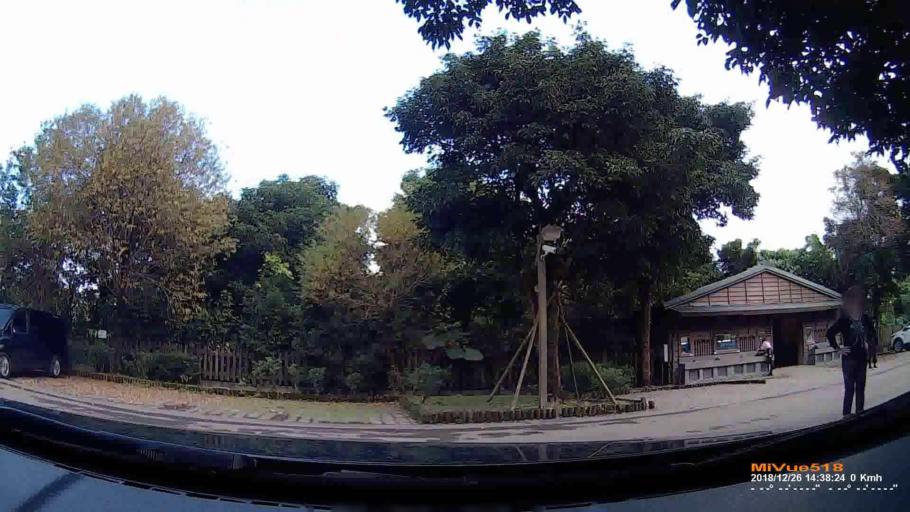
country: TW
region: Taiwan
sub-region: Yilan
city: Yilan
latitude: 24.6807
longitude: 121.7703
